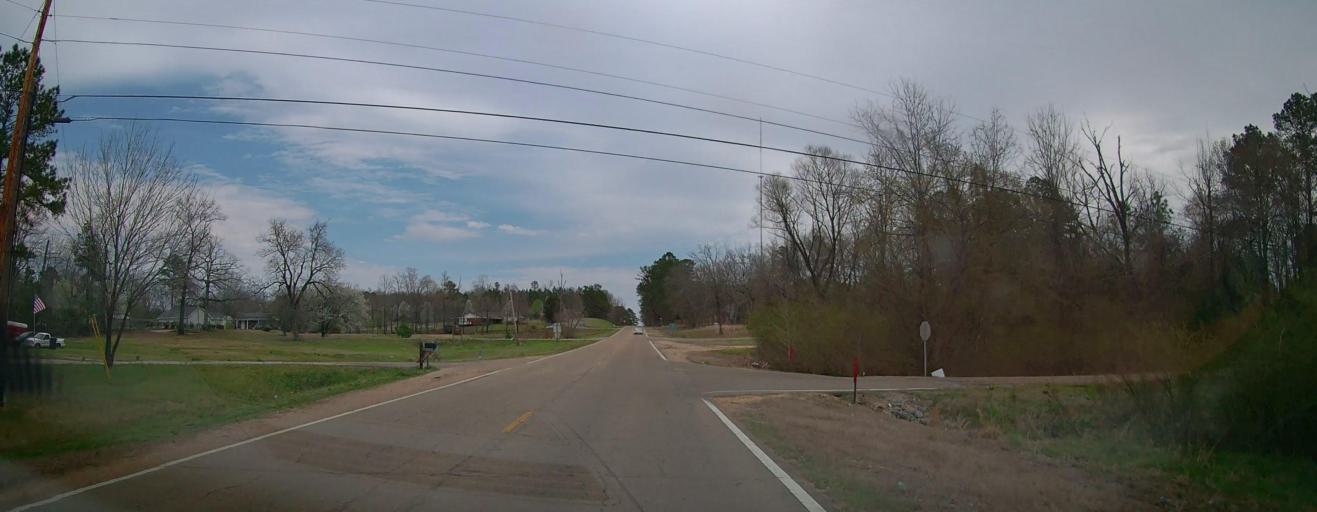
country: US
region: Mississippi
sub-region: Itawamba County
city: Mantachie
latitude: 34.2650
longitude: -88.5460
